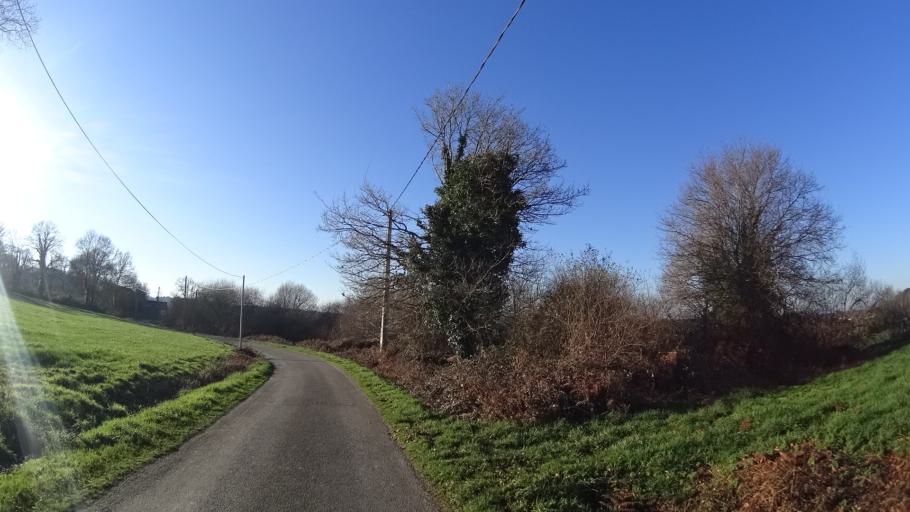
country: FR
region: Brittany
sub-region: Departement du Morbihan
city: Allaire
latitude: 47.6563
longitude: -2.1771
